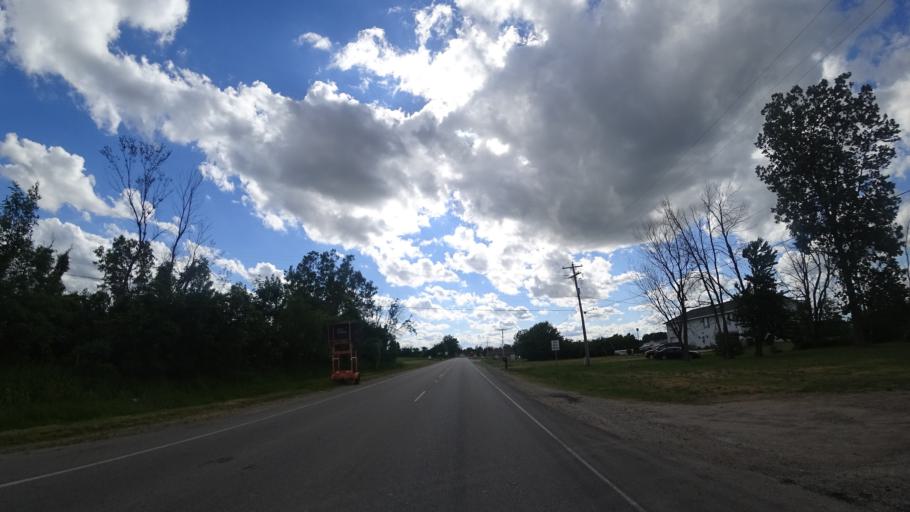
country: US
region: Michigan
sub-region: Ionia County
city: Portland
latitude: 42.8715
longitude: -84.9561
